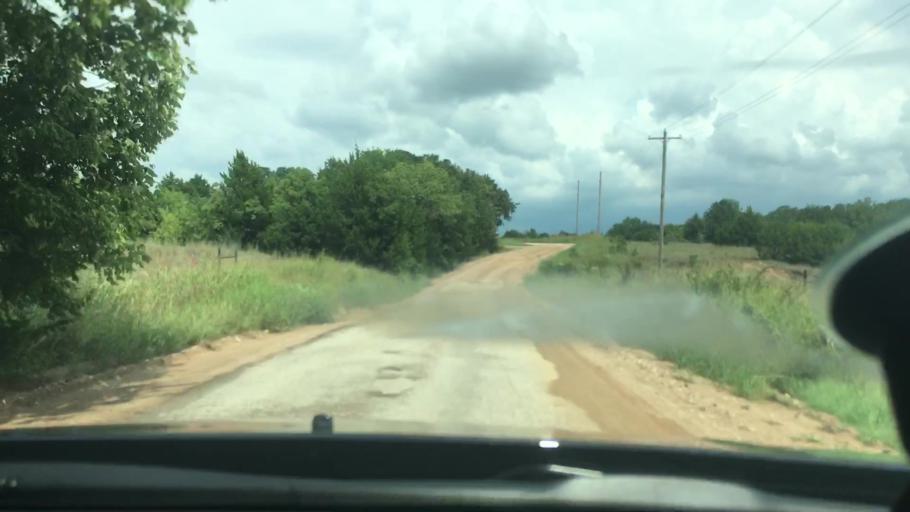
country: US
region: Oklahoma
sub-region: Carter County
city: Dickson
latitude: 34.2477
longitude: -96.9288
